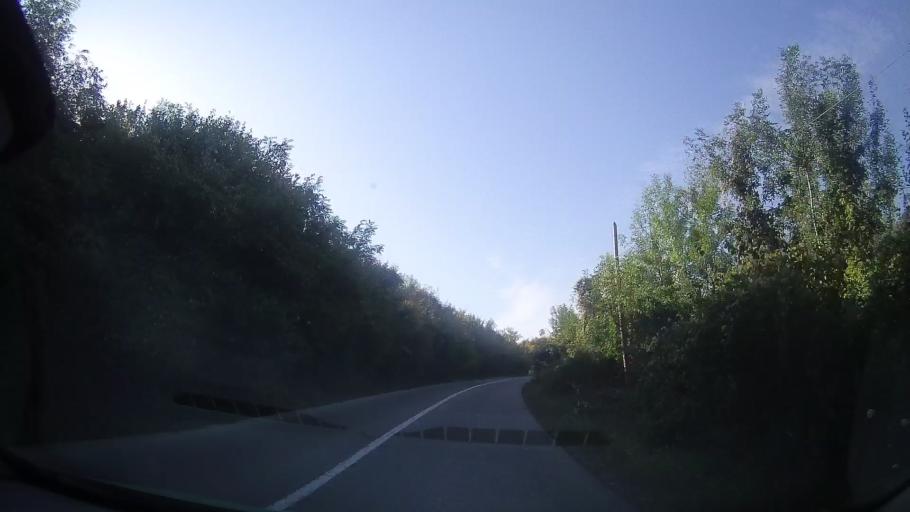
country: RO
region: Timis
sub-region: Oras Recas
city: Recas
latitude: 45.8369
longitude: 21.5217
